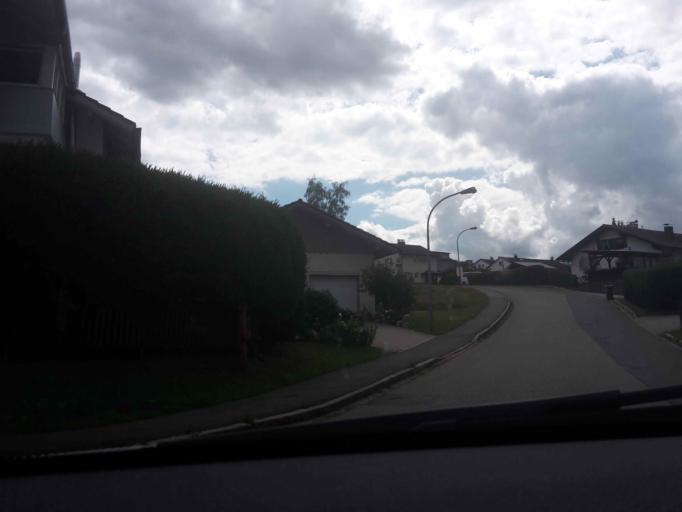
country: DE
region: Bavaria
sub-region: Lower Bavaria
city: Zwiesel
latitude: 49.0230
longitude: 13.2440
